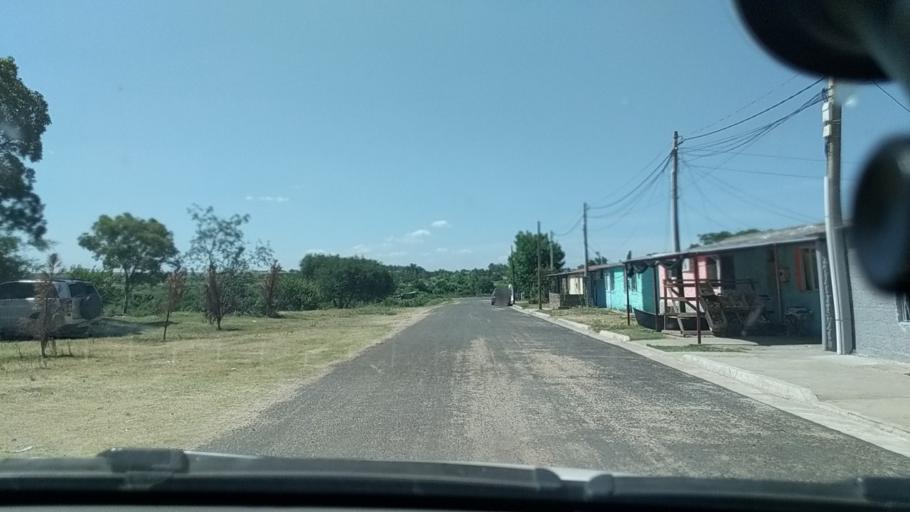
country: UY
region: Tacuarembo
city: Paso de los Toros
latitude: -32.8095
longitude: -56.5320
